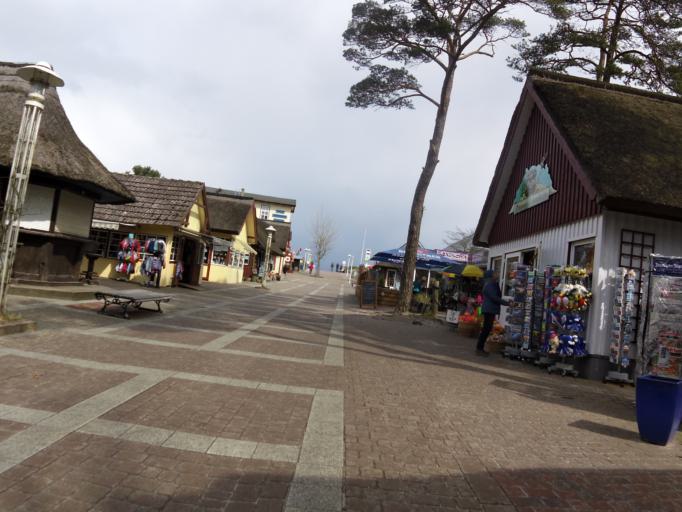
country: DE
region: Mecklenburg-Vorpommern
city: Ostseebad Prerow
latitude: 54.4517
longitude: 12.5697
